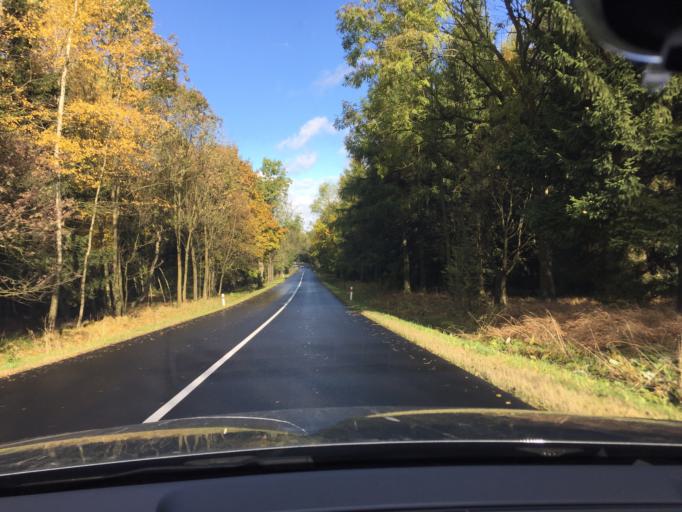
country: CZ
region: Ustecky
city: Libouchec
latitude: 50.7649
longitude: 13.9728
